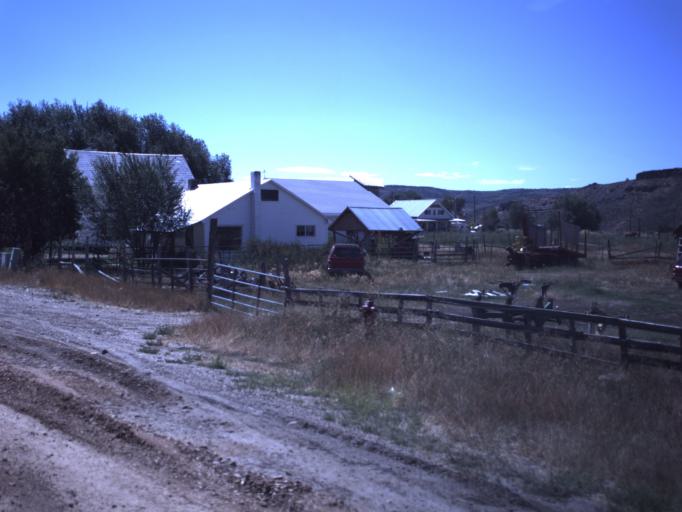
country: US
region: Utah
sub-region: Summit County
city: Francis
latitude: 40.6122
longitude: -111.2807
